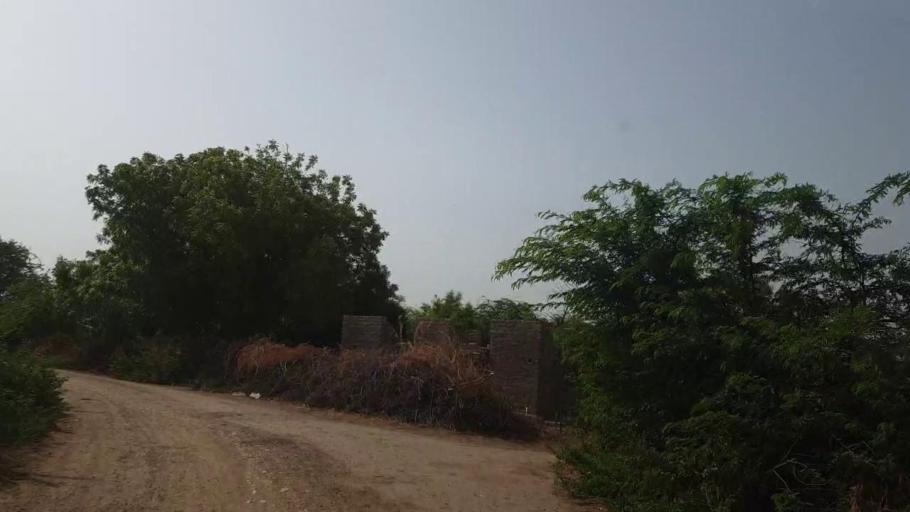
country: PK
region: Sindh
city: Nawabshah
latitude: 26.1147
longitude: 68.4348
